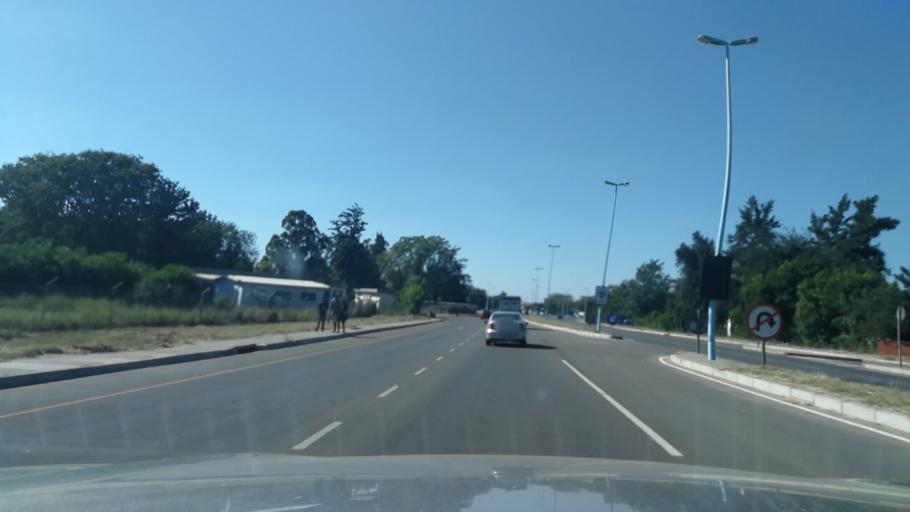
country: BW
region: South East
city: Gaborone
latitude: -24.6749
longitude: 25.9221
